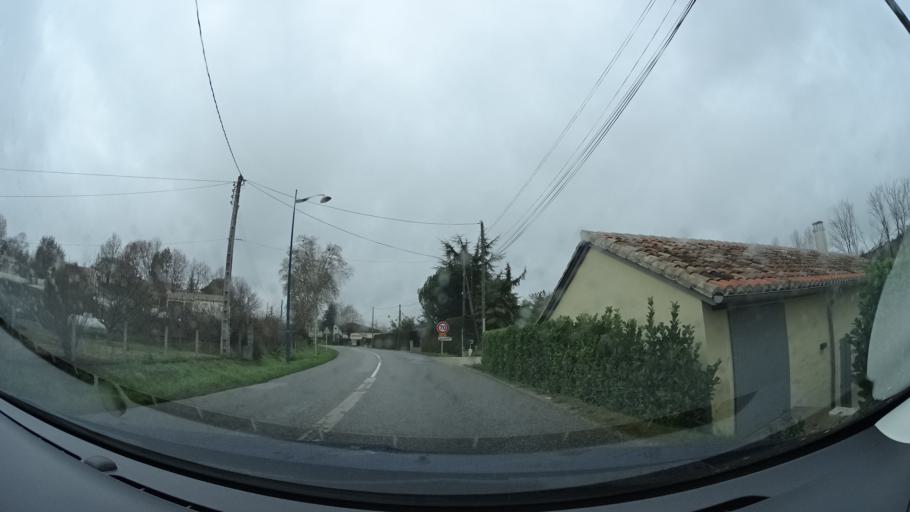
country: FR
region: Midi-Pyrenees
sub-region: Departement du Tarn-et-Garonne
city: Moissac
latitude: 44.1185
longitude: 1.1041
